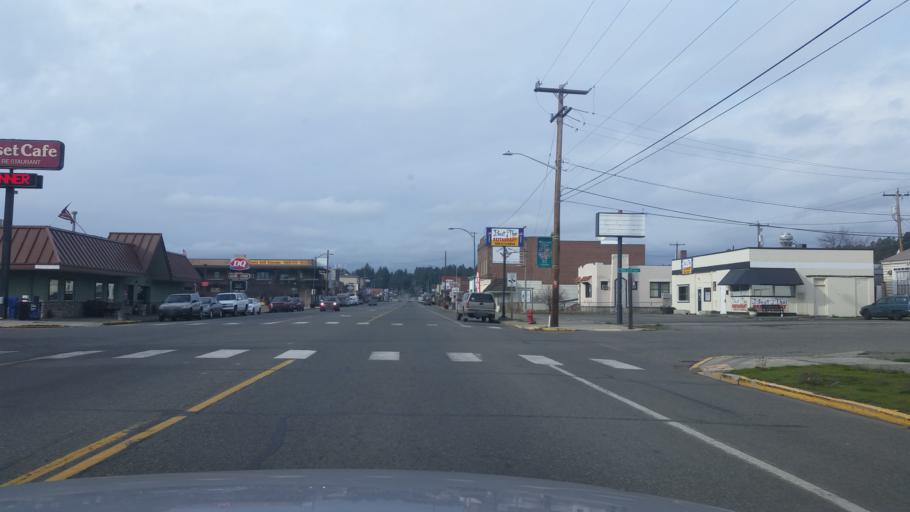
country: US
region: Washington
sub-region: Kittitas County
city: Cle Elum
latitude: 47.1943
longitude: -120.9330
